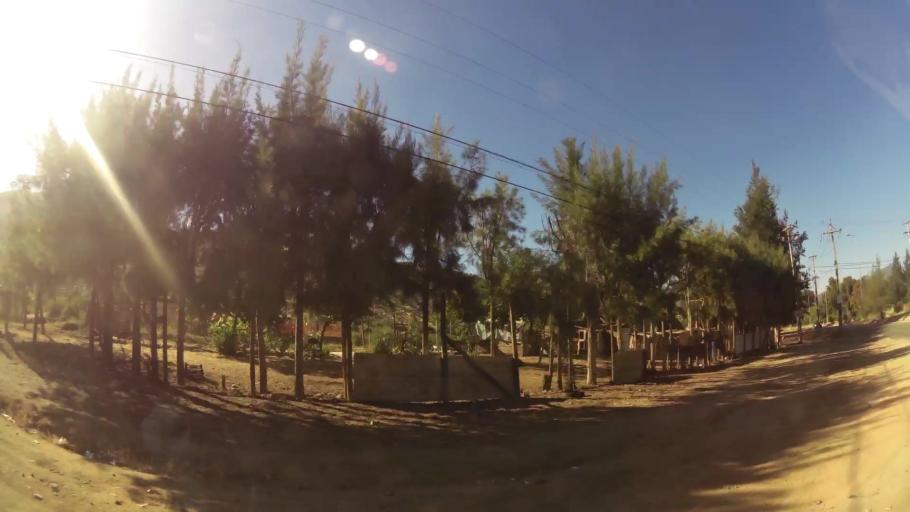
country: CL
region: Santiago Metropolitan
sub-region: Provincia de Chacabuco
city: Lampa
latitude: -33.3902
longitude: -71.1197
